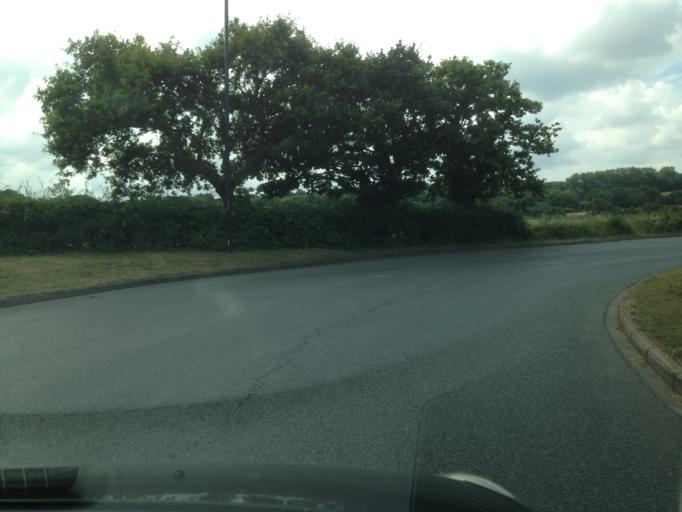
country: GB
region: England
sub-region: Isle of Wight
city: Newport
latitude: 50.7244
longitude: -1.2590
